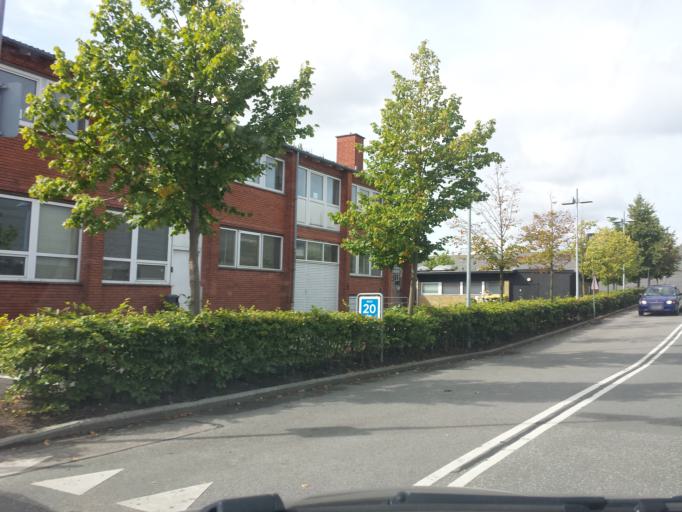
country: DK
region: Capital Region
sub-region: Rodovre Kommune
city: Rodovre
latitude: 55.6790
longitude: 12.4593
